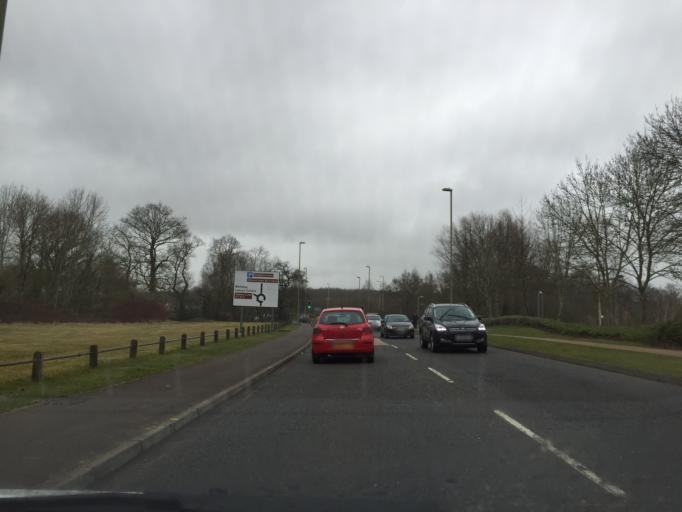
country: GB
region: England
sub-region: Hampshire
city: Botley
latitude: 50.8815
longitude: -1.2441
